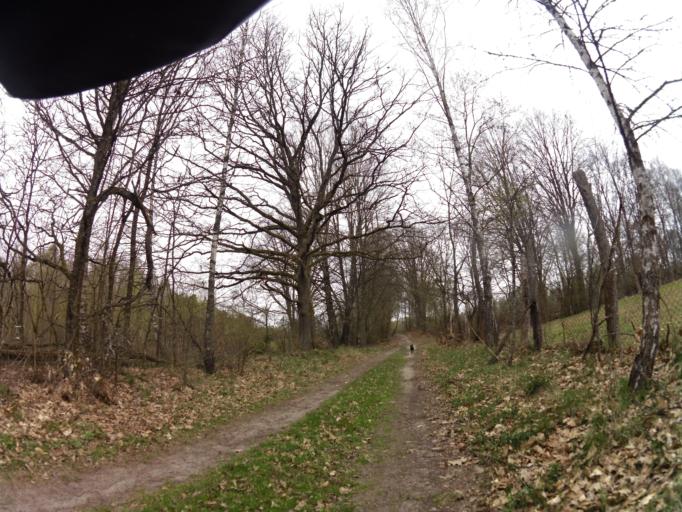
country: PL
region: West Pomeranian Voivodeship
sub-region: Powiat koszalinski
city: Bobolice
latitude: 53.9390
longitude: 16.6973
